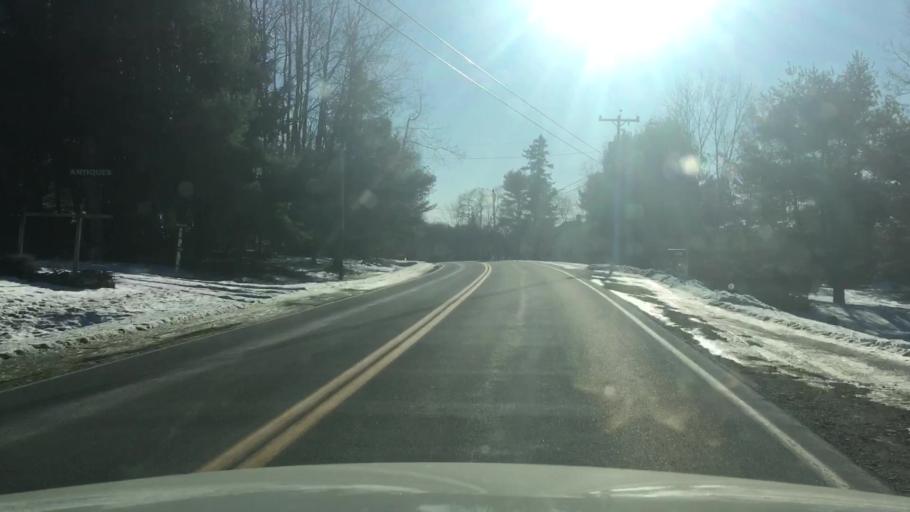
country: US
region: Maine
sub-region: Hancock County
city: Orland
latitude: 44.5433
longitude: -68.7447
